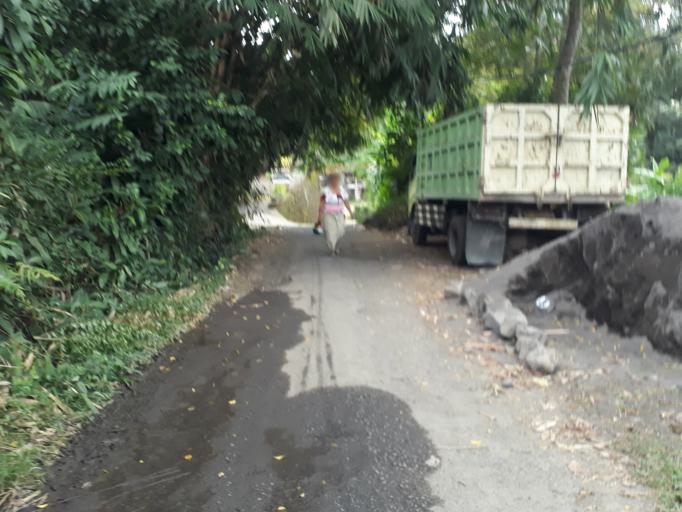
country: ID
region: Bali
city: Banjar Wangsian
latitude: -8.4600
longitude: 115.4372
